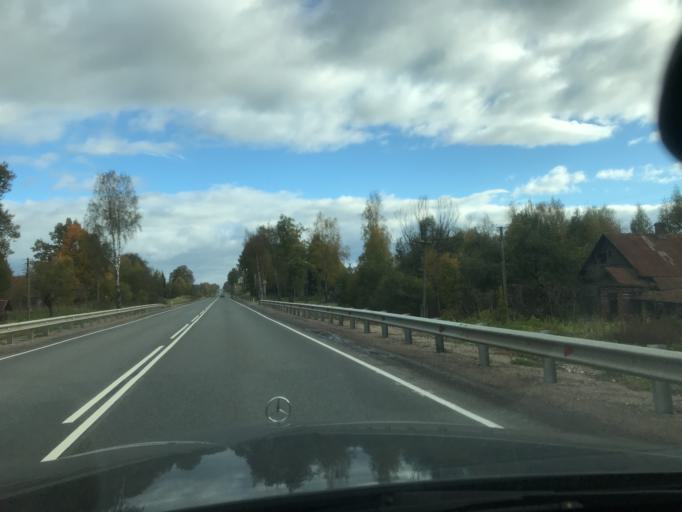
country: RU
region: Pskov
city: Opochka
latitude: 56.6707
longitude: 28.7285
